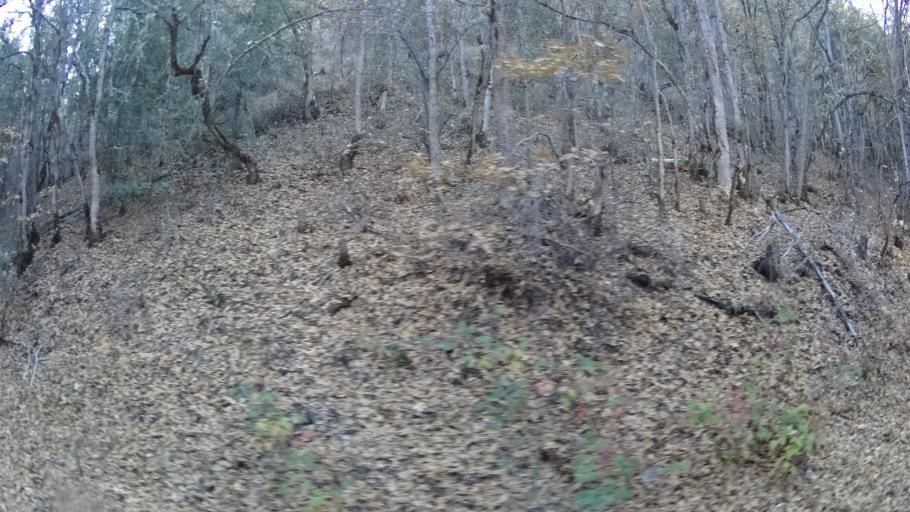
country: US
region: California
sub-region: Siskiyou County
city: Yreka
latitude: 41.8621
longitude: -122.7334
